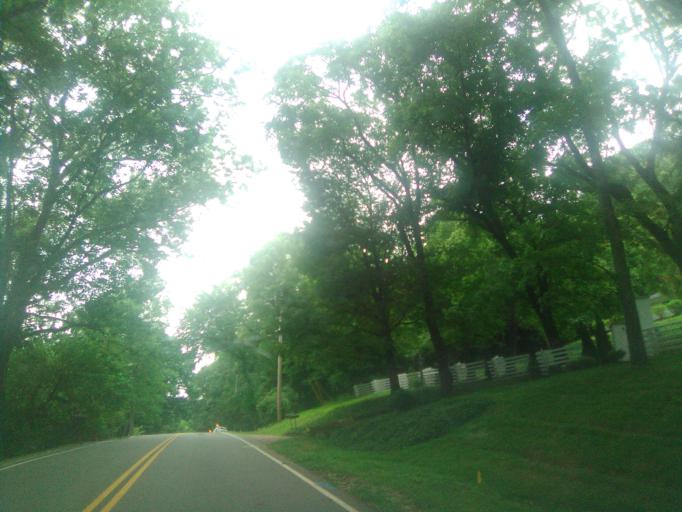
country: US
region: Tennessee
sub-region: Davidson County
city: Forest Hills
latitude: 36.0662
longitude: -86.8499
